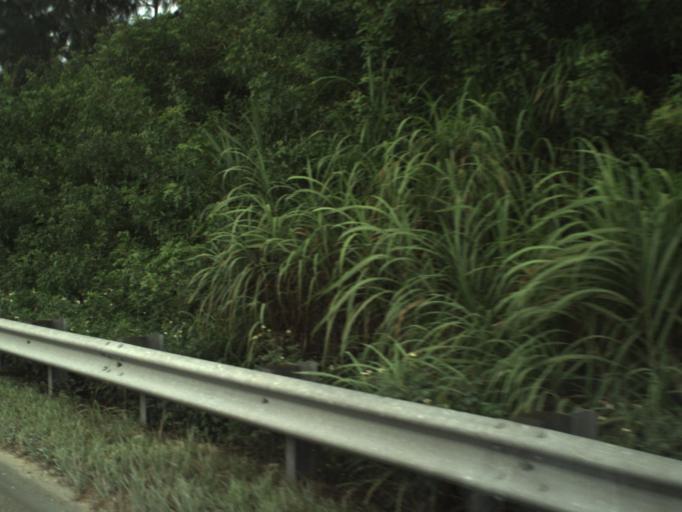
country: US
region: Florida
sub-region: Miami-Dade County
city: The Hammocks
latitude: 25.6924
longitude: -80.4784
